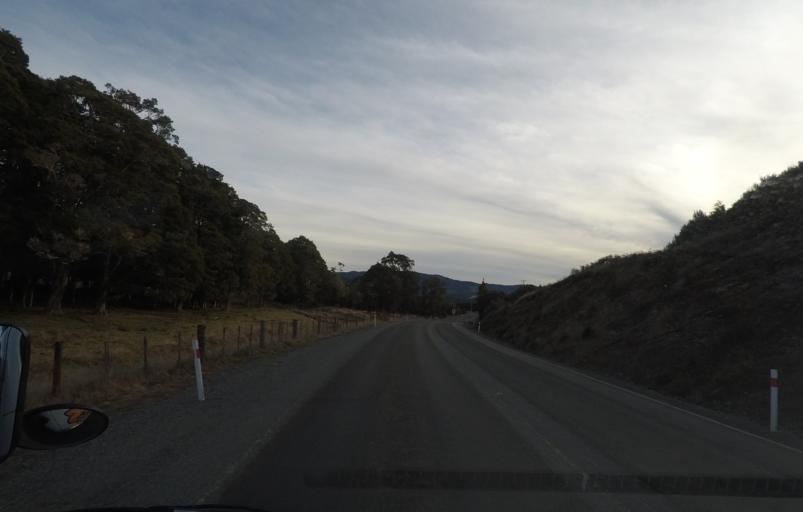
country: NZ
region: Tasman
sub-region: Tasman District
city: Wakefield
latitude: -41.7998
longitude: 172.8646
